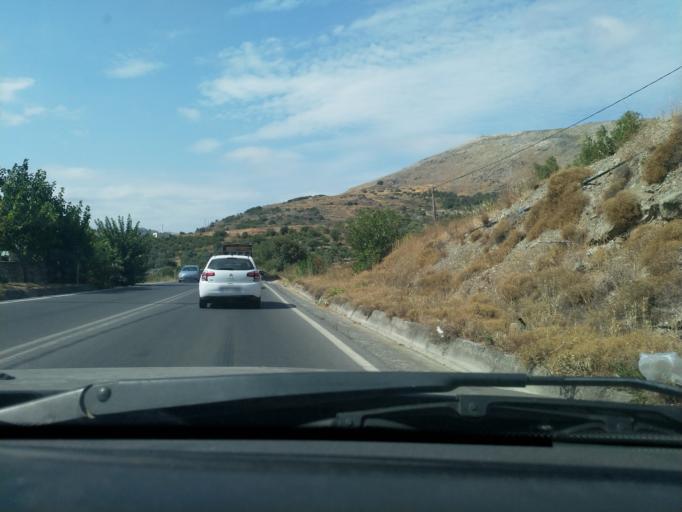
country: GR
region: Crete
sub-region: Nomos Rethymnis
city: Atsipopoulon
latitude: 35.2228
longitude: 24.4863
